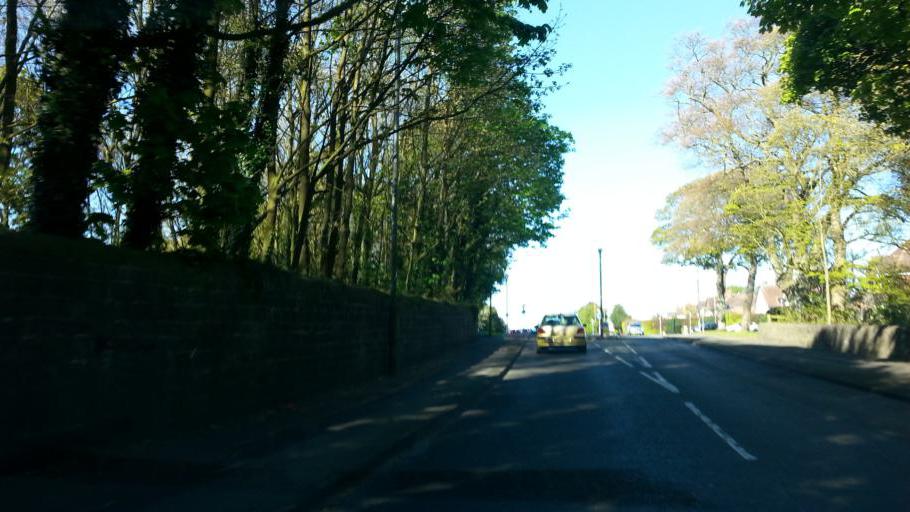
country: GB
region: England
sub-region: Nottinghamshire
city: Mansfield
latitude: 53.1305
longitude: -1.1835
